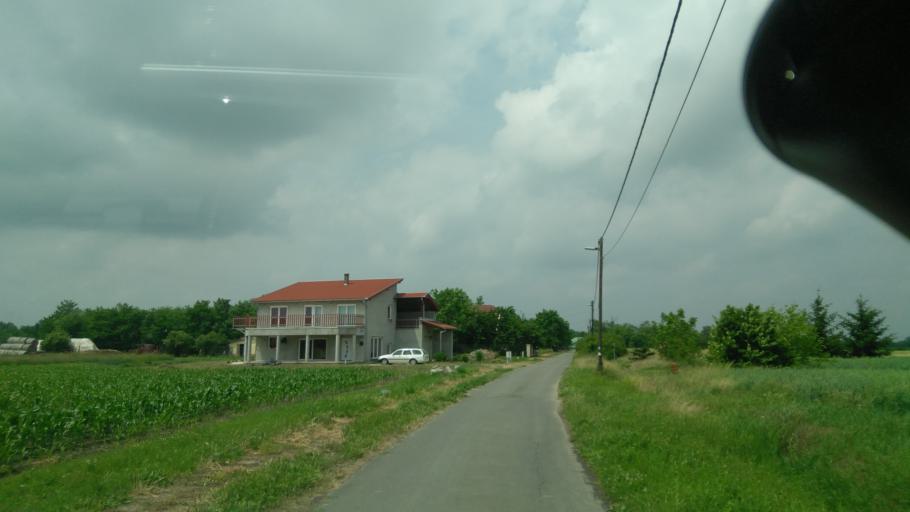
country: HU
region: Bekes
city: Gyula
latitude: 46.6602
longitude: 21.2558
